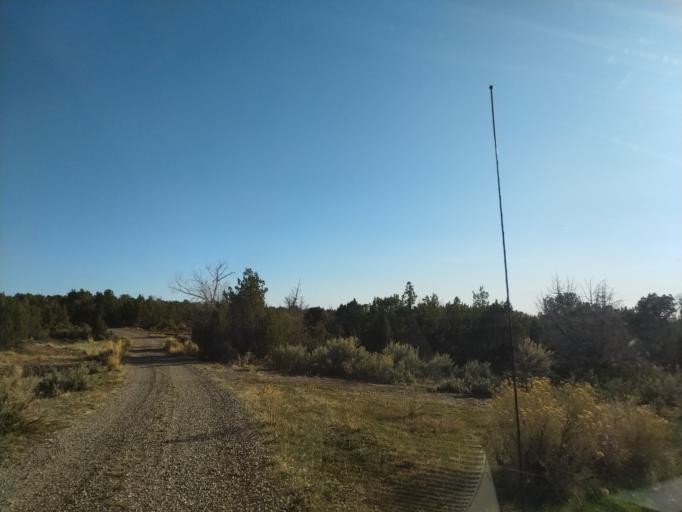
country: US
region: Colorado
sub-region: Mesa County
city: Loma
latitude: 38.9535
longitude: -109.0610
